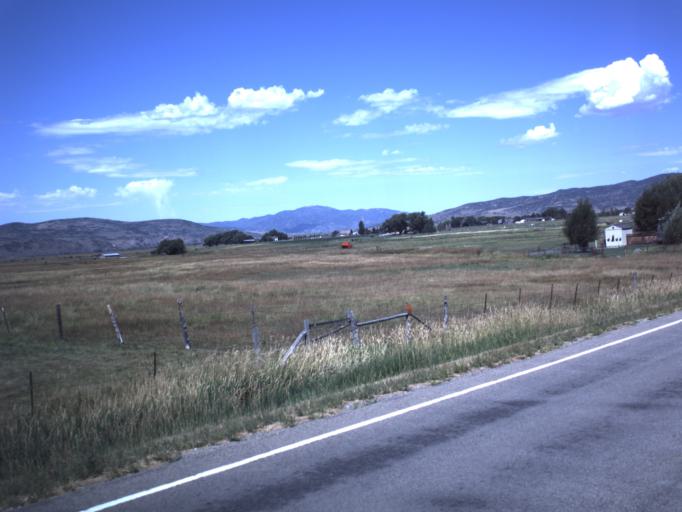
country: US
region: Utah
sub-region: Summit County
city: Kamas
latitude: 40.6654
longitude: -111.2808
